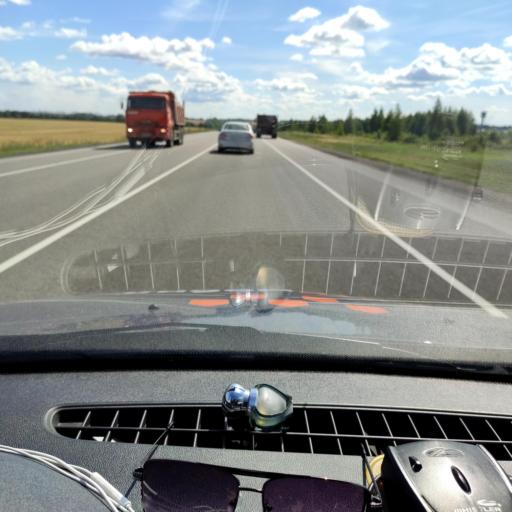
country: RU
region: Lipetsk
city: Borinskoye
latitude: 52.4743
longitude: 39.3768
